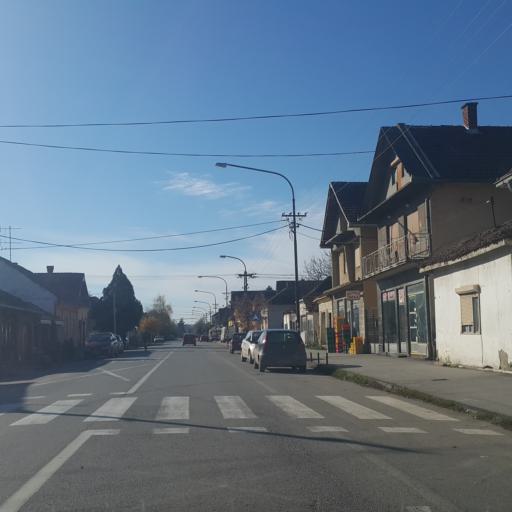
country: RS
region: Central Serbia
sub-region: Sumadijski Okrug
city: Topola
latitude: 44.2535
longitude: 20.8051
